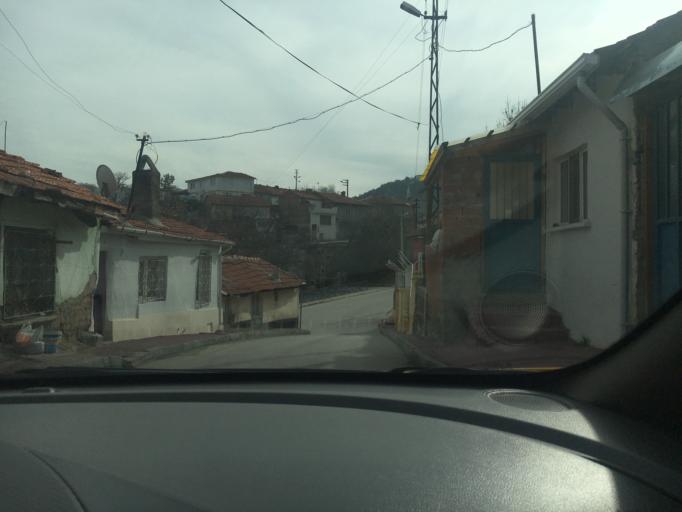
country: TR
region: Eskisehir
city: Eskisehir
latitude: 39.7619
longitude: 30.5281
